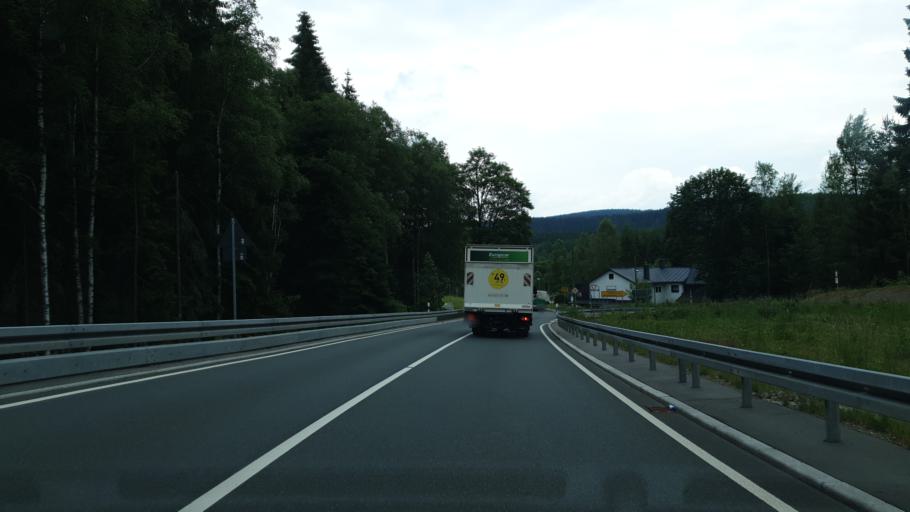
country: DE
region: Saxony
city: Tannenbergsthal
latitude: 50.4537
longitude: 12.4636
